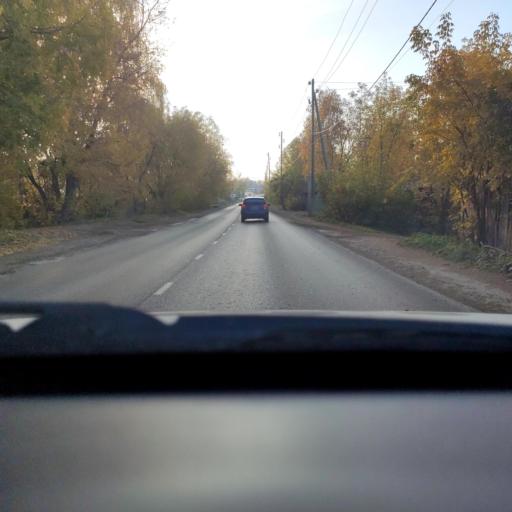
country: RU
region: Perm
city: Kondratovo
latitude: 57.9631
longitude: 56.1296
